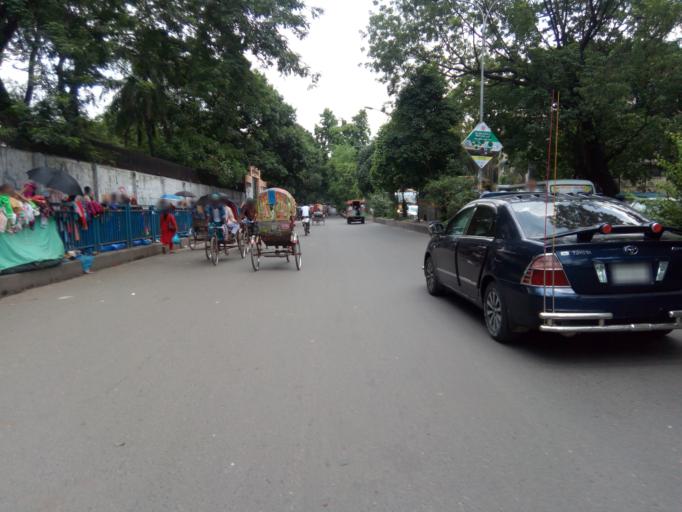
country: BD
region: Dhaka
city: Azimpur
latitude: 23.7310
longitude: 90.3856
